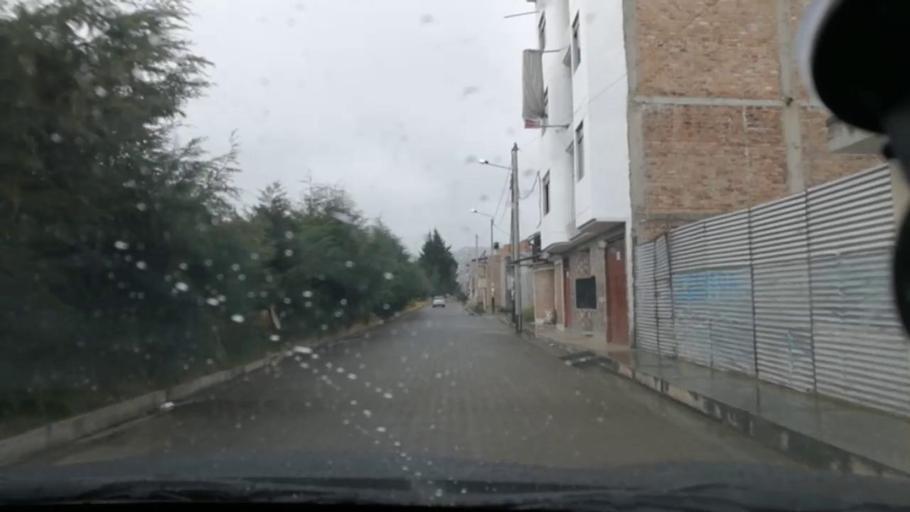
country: PE
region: Cajamarca
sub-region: Provincia de Cajamarca
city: Cajamarca
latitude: -7.1635
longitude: -78.4703
